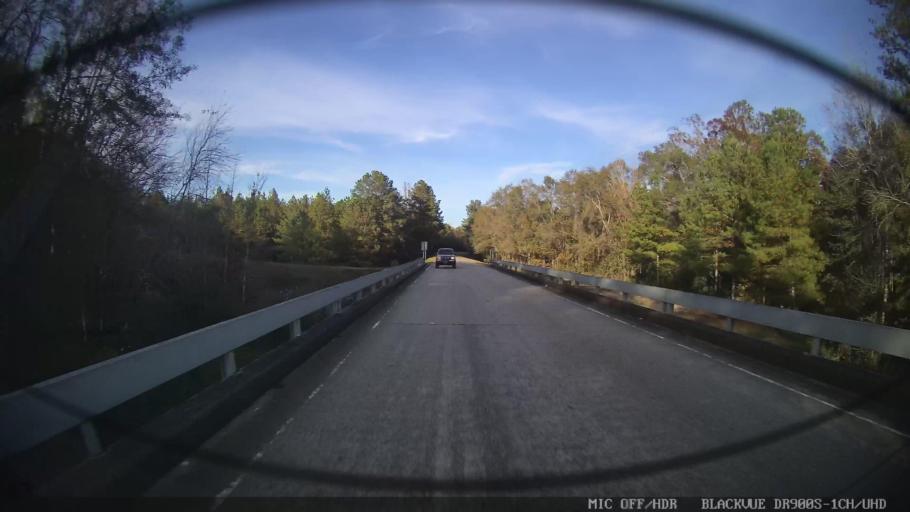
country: US
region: Mississippi
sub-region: Lamar County
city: Purvis
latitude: 31.1564
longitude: -89.3330
